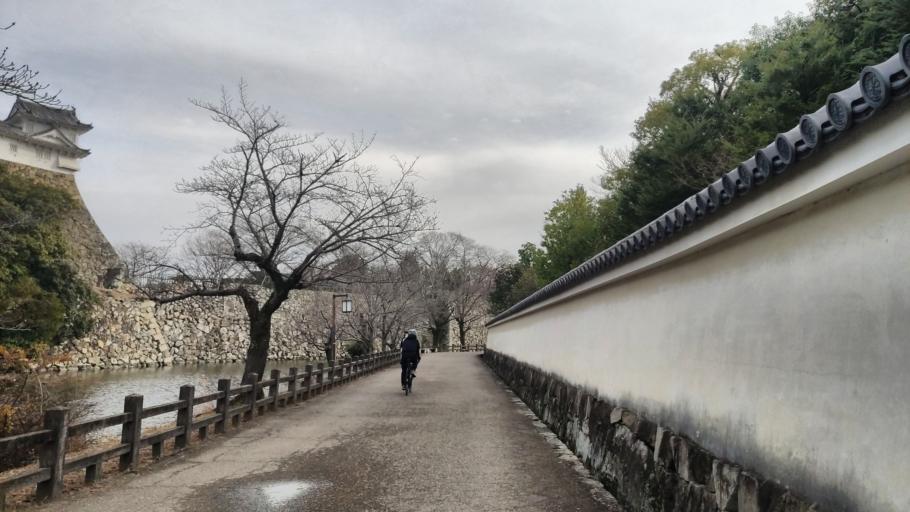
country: JP
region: Hyogo
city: Himeji
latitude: 34.8386
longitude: 134.6903
